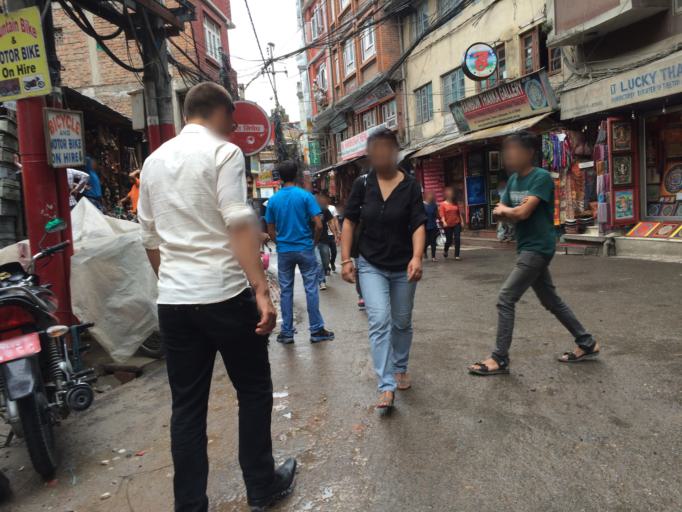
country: NP
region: Central Region
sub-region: Bagmati Zone
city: Kathmandu
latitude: 27.7146
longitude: 85.3113
